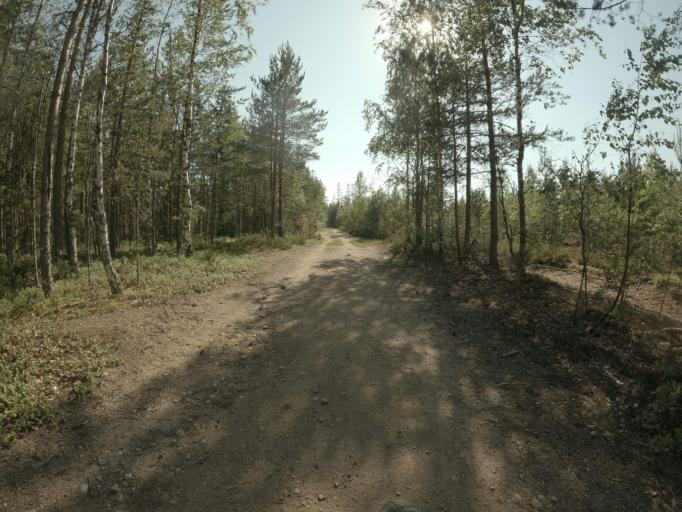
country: RU
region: Leningrad
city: Yakovlevo
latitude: 60.4549
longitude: 29.2649
